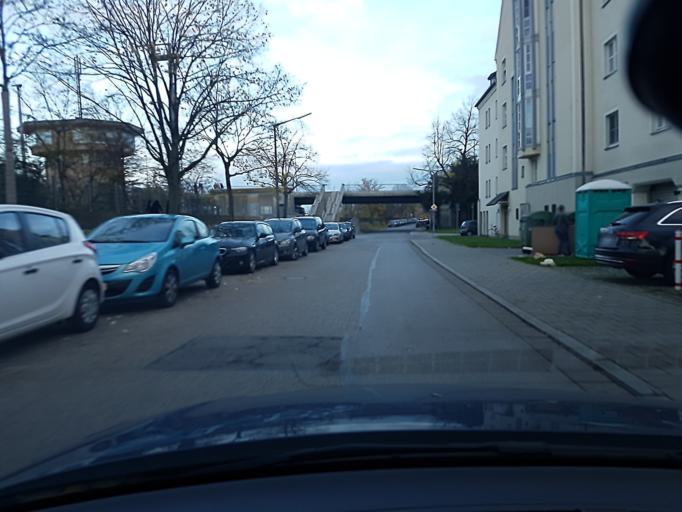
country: DE
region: Bavaria
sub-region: Upper Palatinate
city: Lappersdorf
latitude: 49.0263
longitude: 12.0977
